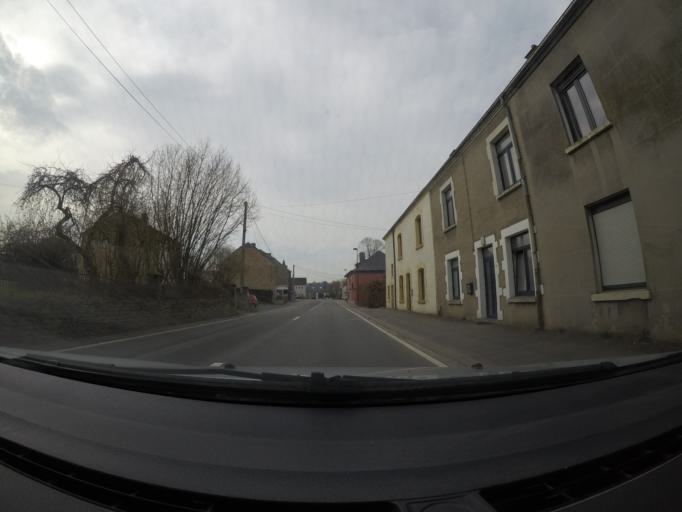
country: BE
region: Wallonia
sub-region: Province du Luxembourg
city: Chiny
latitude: 49.6958
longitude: 5.4145
